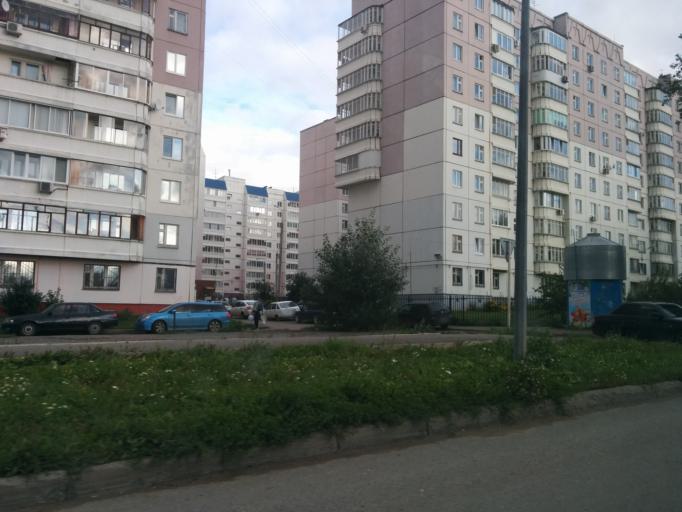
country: RU
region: Perm
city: Perm
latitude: 58.0033
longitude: 56.2978
